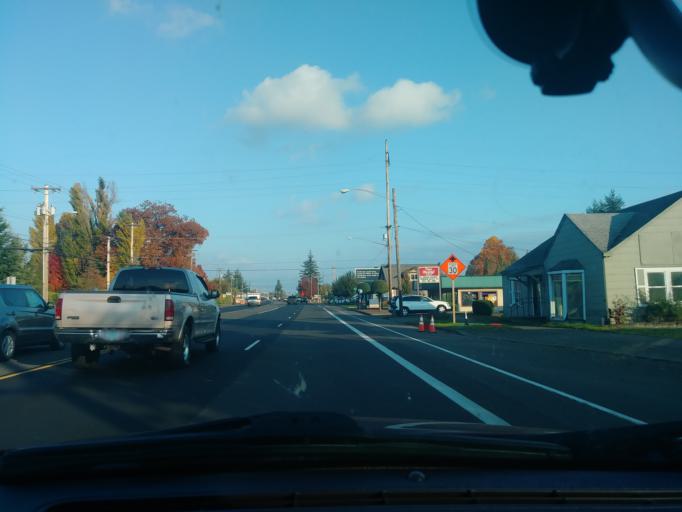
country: US
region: Oregon
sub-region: Washington County
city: Forest Grove
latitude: 45.5201
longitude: -123.0892
